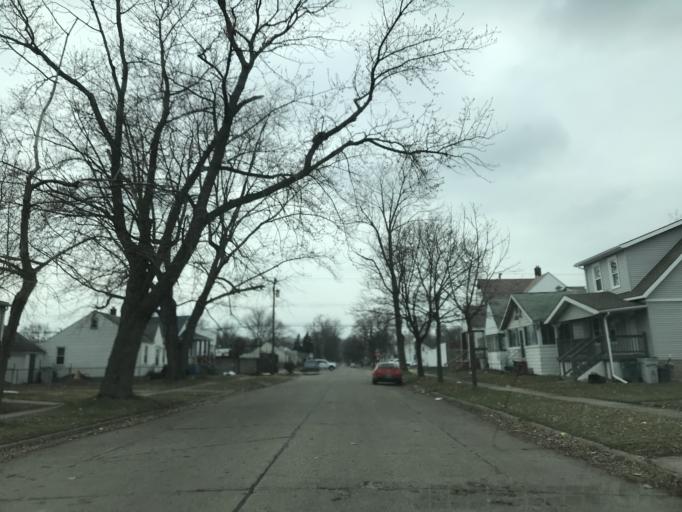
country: US
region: Michigan
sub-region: Oakland County
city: Hazel Park
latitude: 42.4502
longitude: -83.1016
